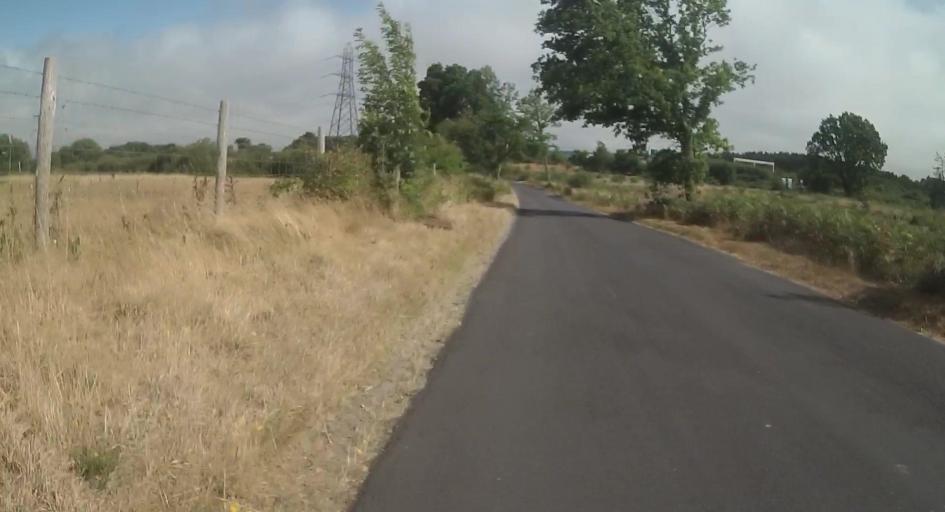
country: GB
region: England
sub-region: Dorset
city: Bovington Camp
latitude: 50.6885
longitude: -2.2655
